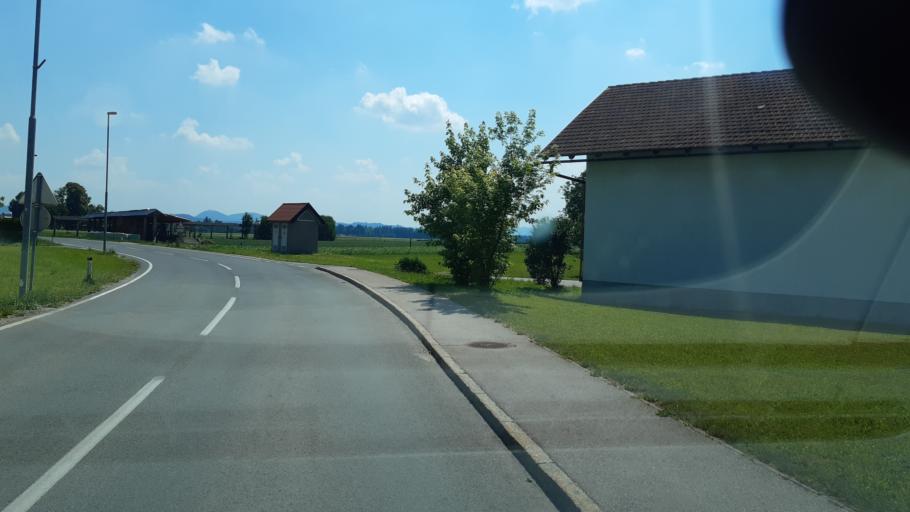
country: SI
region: Cerklje na Gorenjskem
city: Cerklje na Gorenjskem
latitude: 46.2385
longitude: 14.4847
